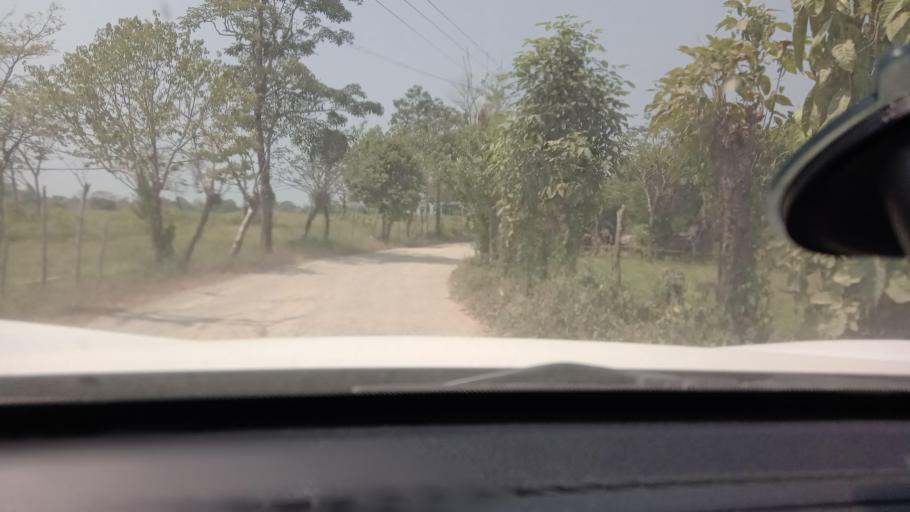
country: MX
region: Tabasco
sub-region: Huimanguillo
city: Francisco Rueda
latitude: 17.5100
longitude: -93.8969
